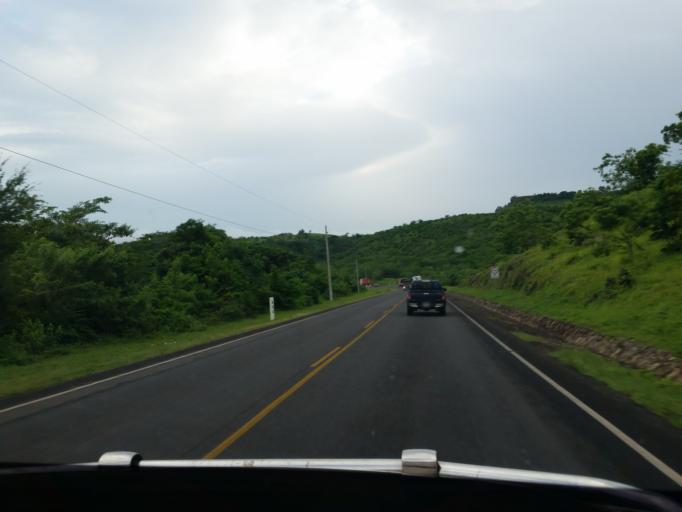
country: NI
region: Boaco
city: Teustepe
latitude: 12.4623
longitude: -86.0408
